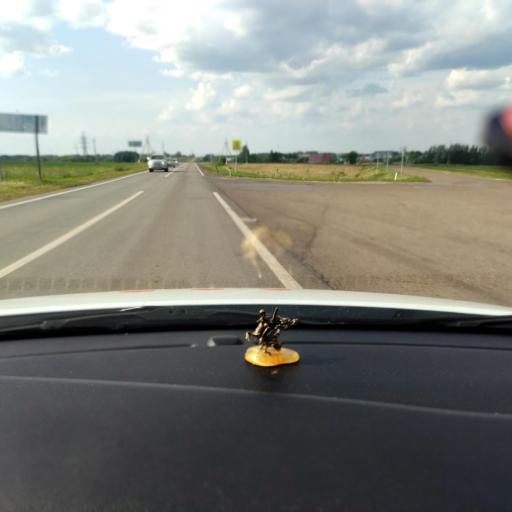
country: RU
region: Tatarstan
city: Stolbishchi
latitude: 55.4784
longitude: 49.2938
